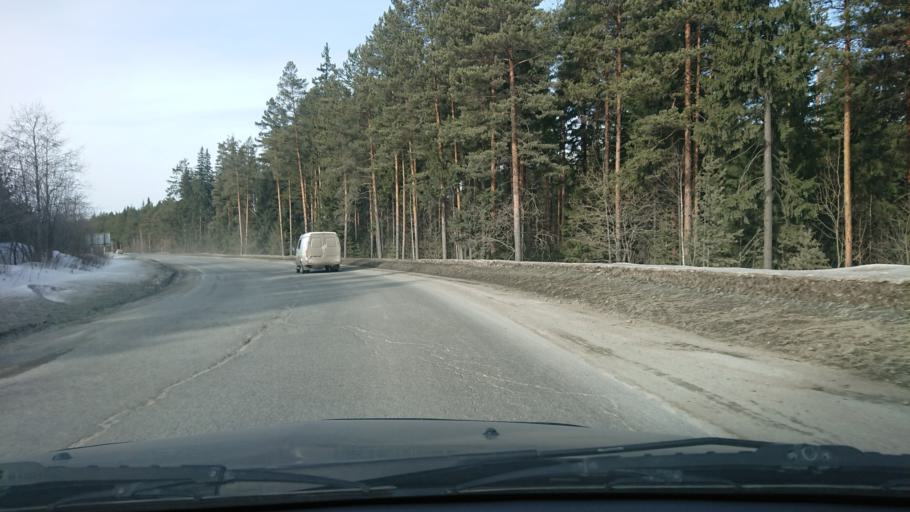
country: RU
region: Sverdlovsk
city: Revda
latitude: 56.7970
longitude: 59.9987
